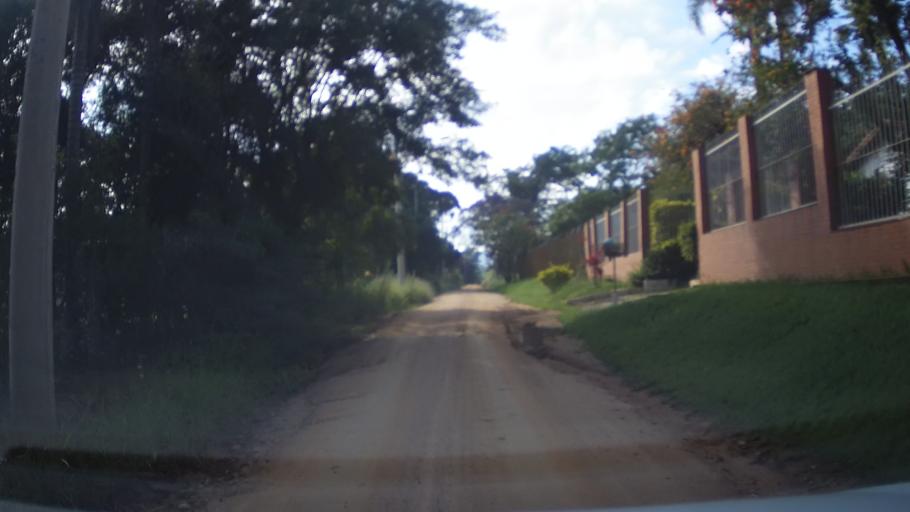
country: BR
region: Sao Paulo
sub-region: Itupeva
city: Itupeva
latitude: -23.2178
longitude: -47.0661
